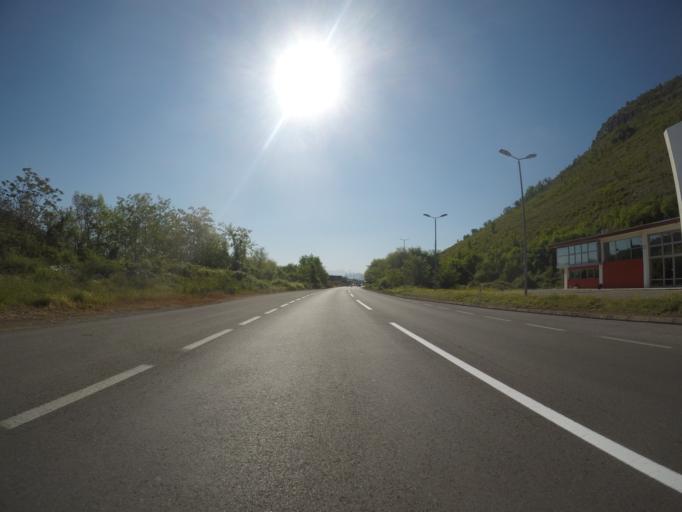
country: ME
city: Spuz
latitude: 42.4539
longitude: 19.1930
